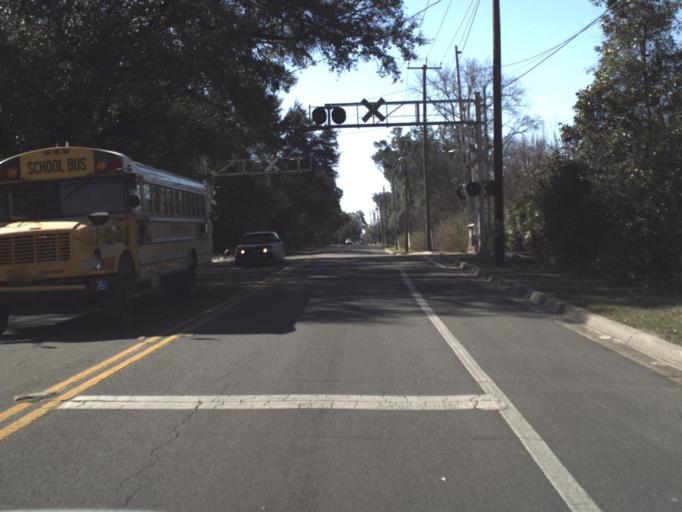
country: US
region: Florida
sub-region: Bay County
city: Cedar Grove
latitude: 30.1626
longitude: -85.6251
